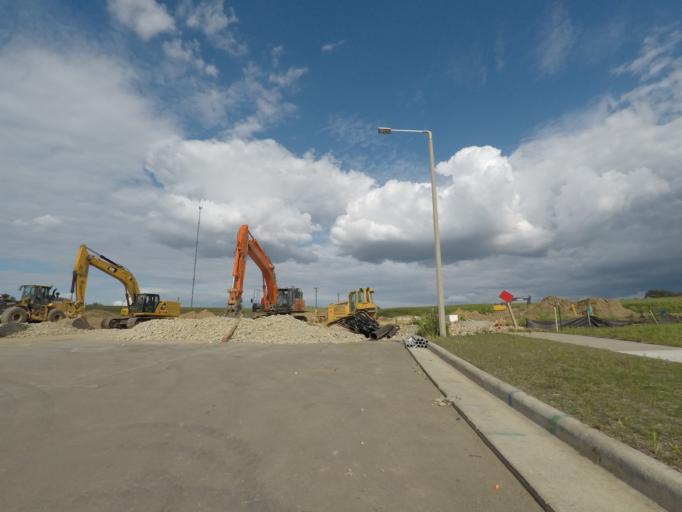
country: US
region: Wisconsin
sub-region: Dane County
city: Verona
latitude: 43.0509
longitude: -89.5487
